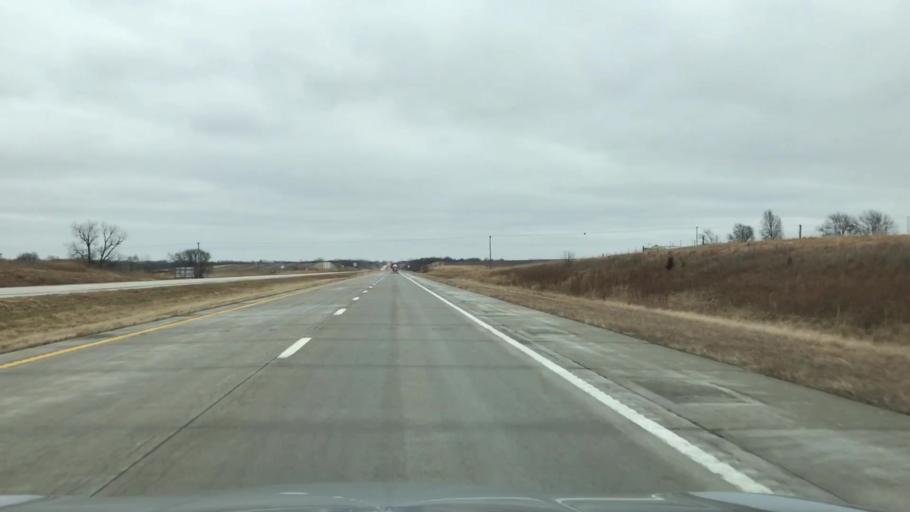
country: US
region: Missouri
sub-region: Caldwell County
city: Hamilton
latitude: 39.7337
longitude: -93.9869
